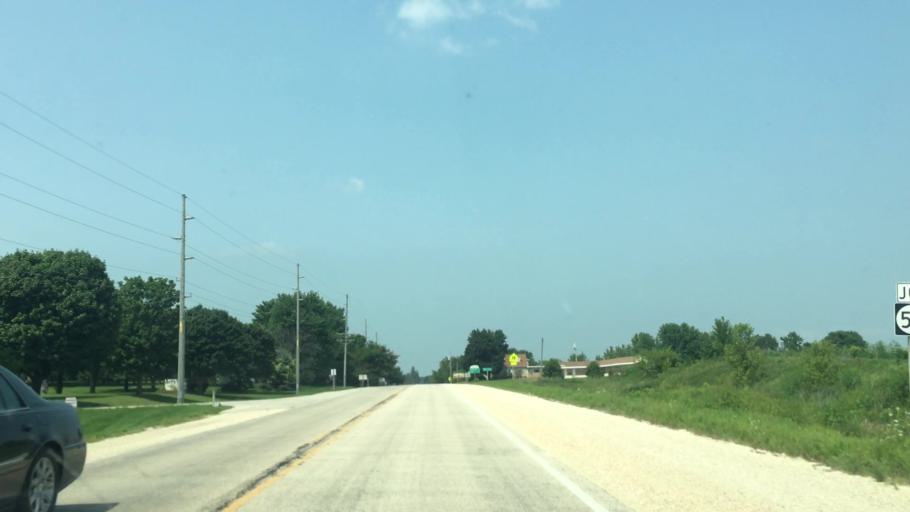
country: US
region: Iowa
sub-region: Fayette County
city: West Union
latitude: 42.9481
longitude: -91.8142
